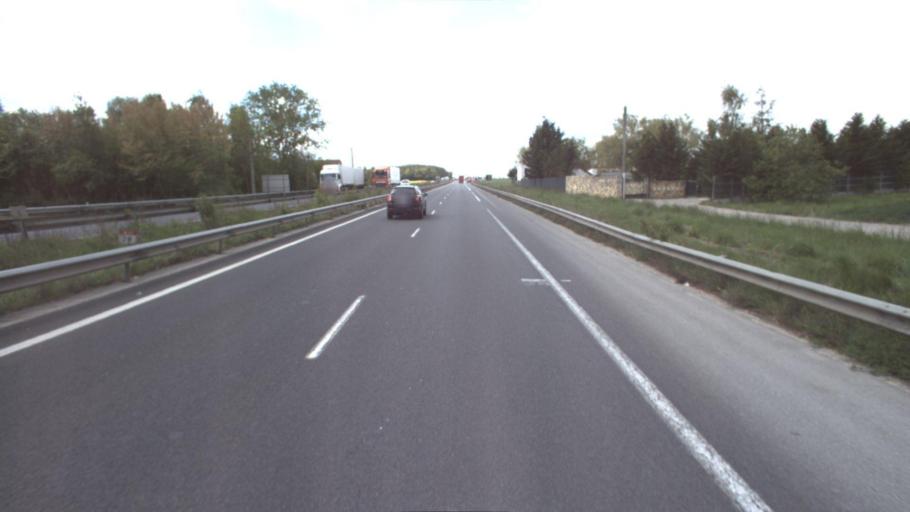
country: FR
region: Ile-de-France
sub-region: Departement de Seine-et-Marne
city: Rozay-en-Brie
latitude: 48.6891
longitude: 2.9244
